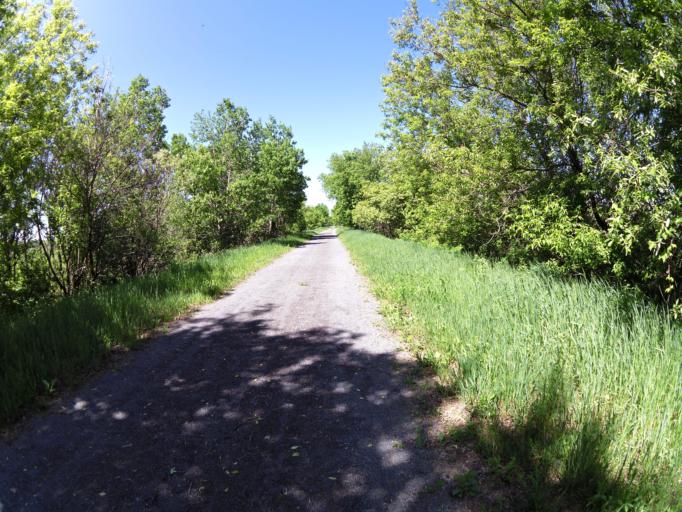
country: CA
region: Ontario
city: Clarence-Rockland
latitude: 45.4262
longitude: -75.3169
